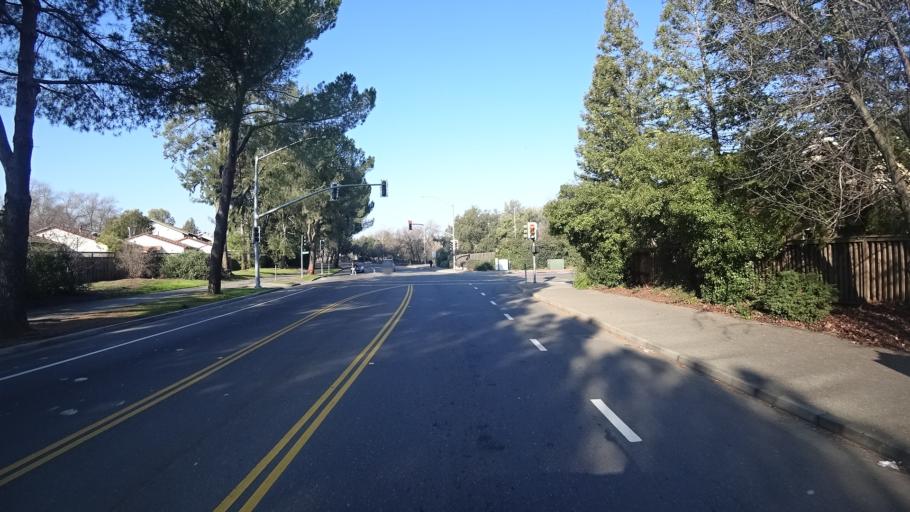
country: US
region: California
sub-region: Yolo County
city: Davis
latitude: 38.5535
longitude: -121.7811
